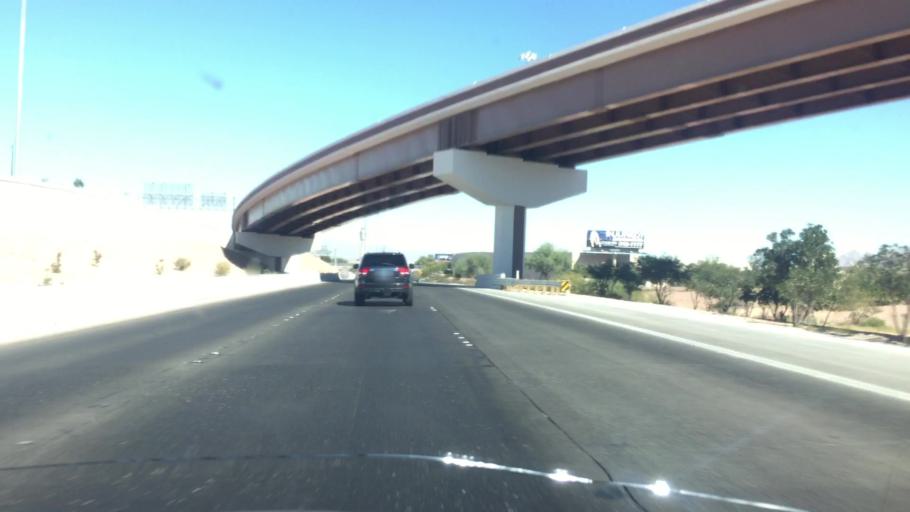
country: US
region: Nevada
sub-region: Clark County
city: Paradise
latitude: 36.0632
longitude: -115.1493
